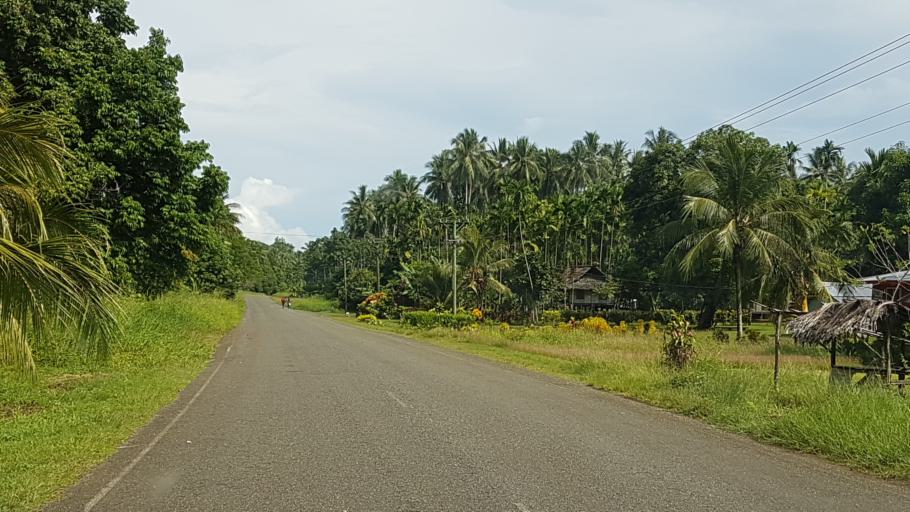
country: PG
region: Madang
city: Madang
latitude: -5.0025
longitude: 145.7908
